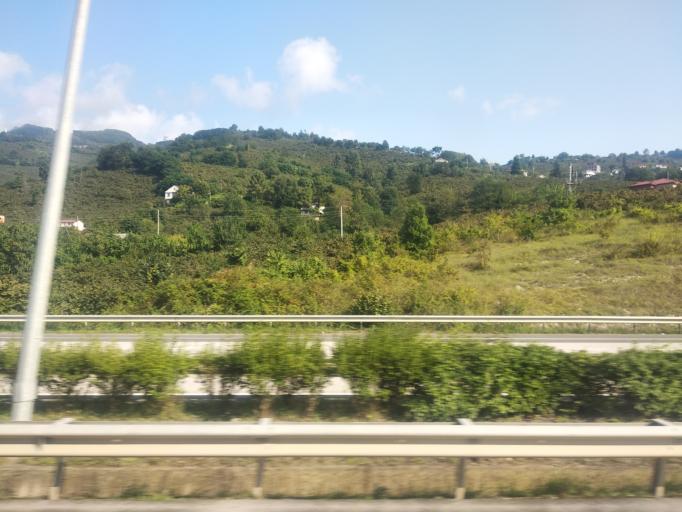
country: TR
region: Ordu
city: Ordu
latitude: 41.0046
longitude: 37.8267
